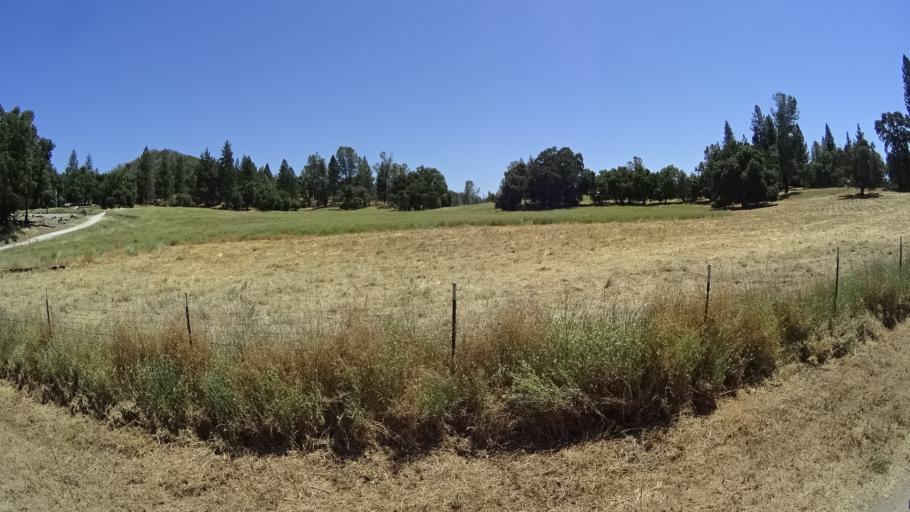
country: US
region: California
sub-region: Calaveras County
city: Mountain Ranch
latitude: 38.2269
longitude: -120.5408
